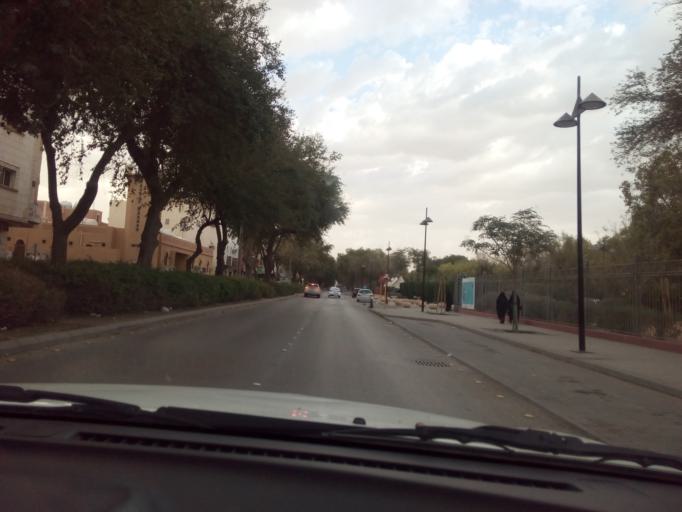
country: SA
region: Ar Riyad
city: Riyadh
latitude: 24.6463
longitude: 46.7073
